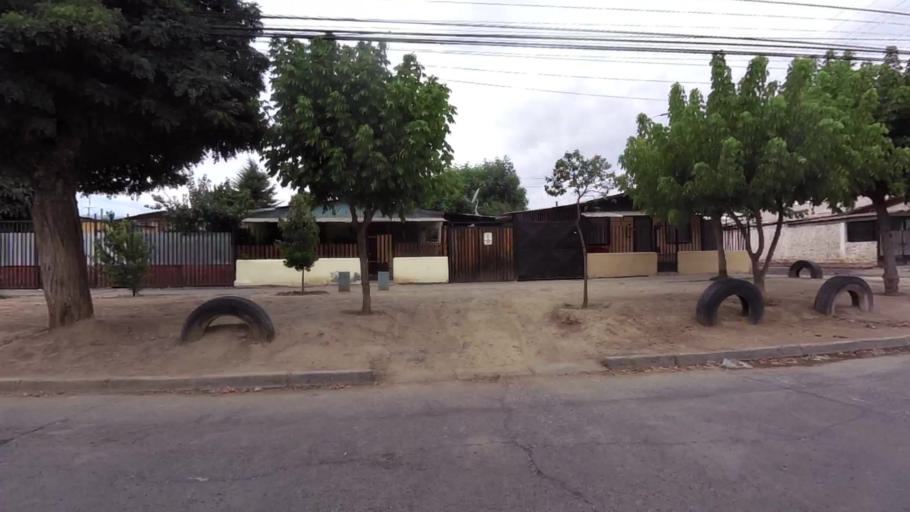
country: CL
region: O'Higgins
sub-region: Provincia de Cachapoal
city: Graneros
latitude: -34.0741
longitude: -70.7250
